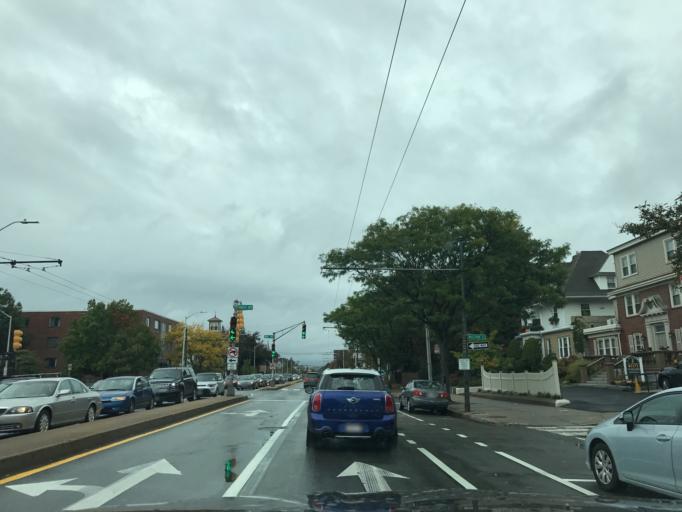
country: US
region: Massachusetts
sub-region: Middlesex County
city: Somerville
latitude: 42.3924
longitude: -71.1245
